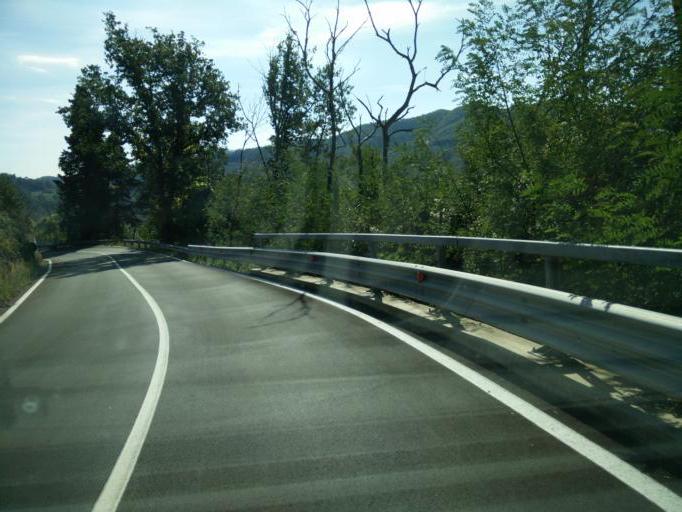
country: IT
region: Liguria
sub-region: Provincia di La Spezia
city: Carrodano
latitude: 44.2456
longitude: 9.6503
